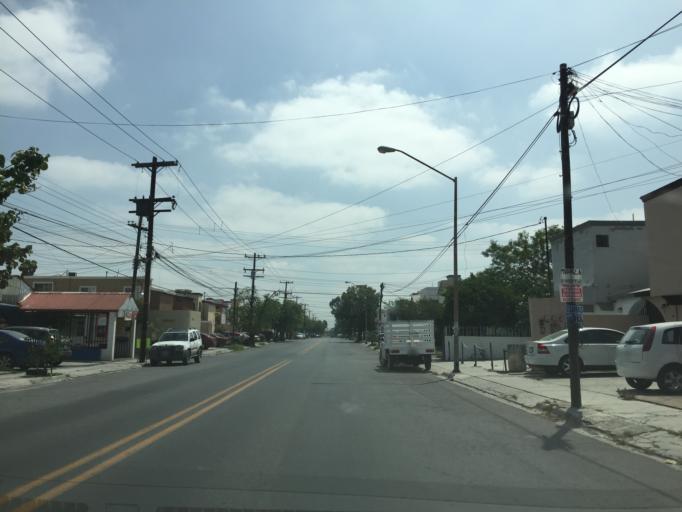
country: MX
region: Nuevo Leon
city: Guadalupe
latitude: 25.7067
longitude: -100.2293
